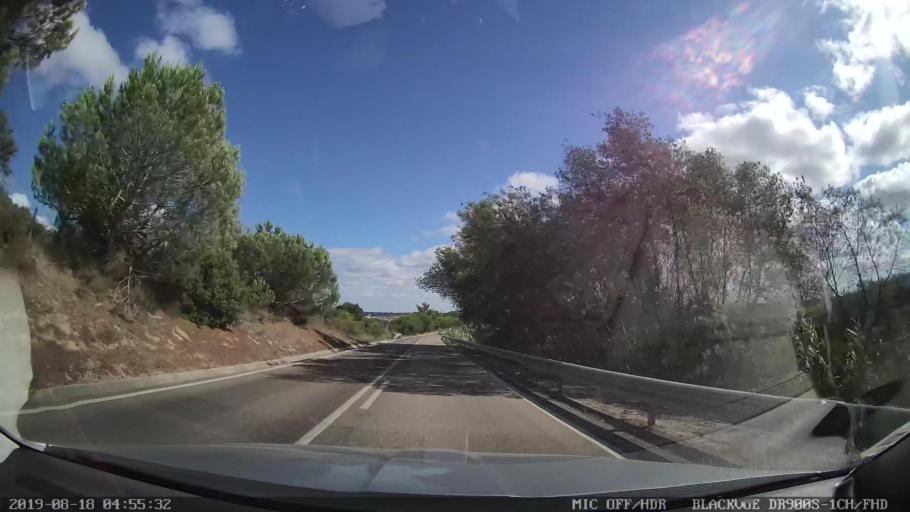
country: PT
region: Santarem
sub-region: Benavente
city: Poceirao
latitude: 38.8740
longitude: -8.7471
